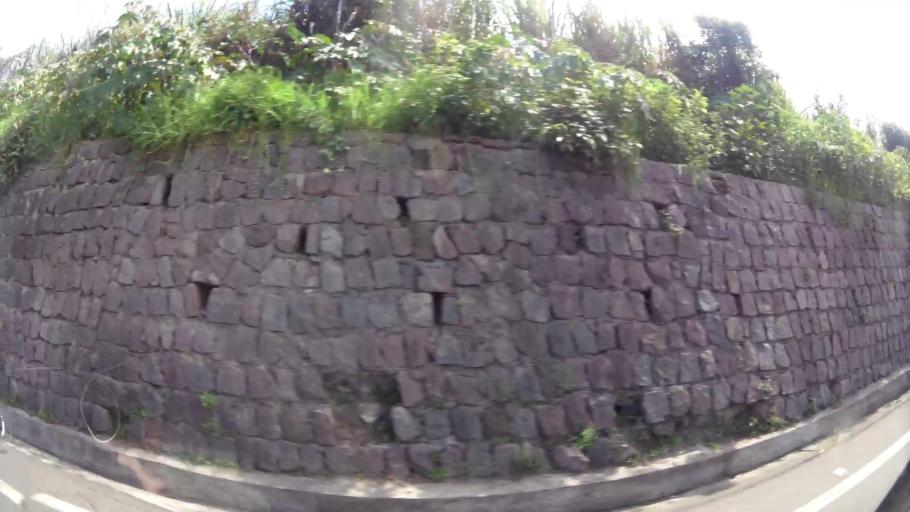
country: EC
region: Pichincha
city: Quito
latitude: -0.2035
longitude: -78.4304
